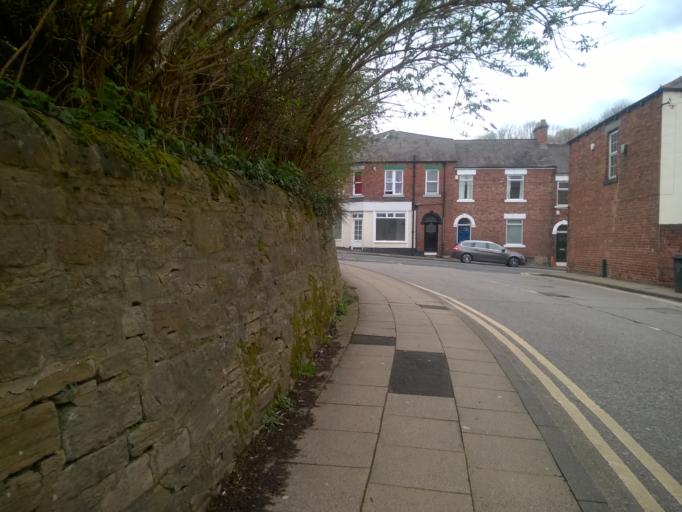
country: GB
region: England
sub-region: County Durham
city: Durham
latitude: 54.7762
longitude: -1.5843
